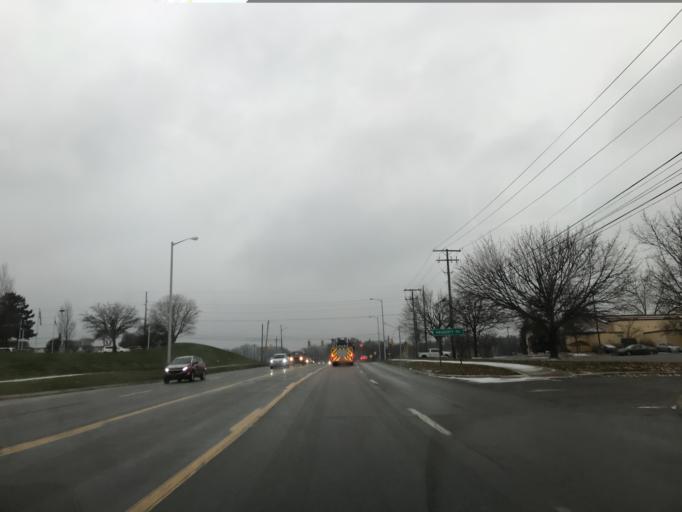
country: US
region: Michigan
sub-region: Wayne County
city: Northville
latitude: 42.4250
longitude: -83.4308
